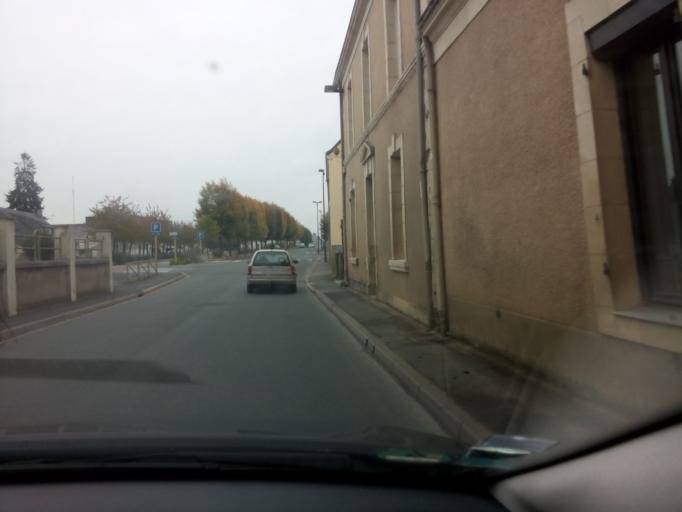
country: FR
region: Pays de la Loire
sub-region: Departement de Maine-et-Loire
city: Seiches-sur-le-Loir
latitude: 47.5749
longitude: -0.3599
